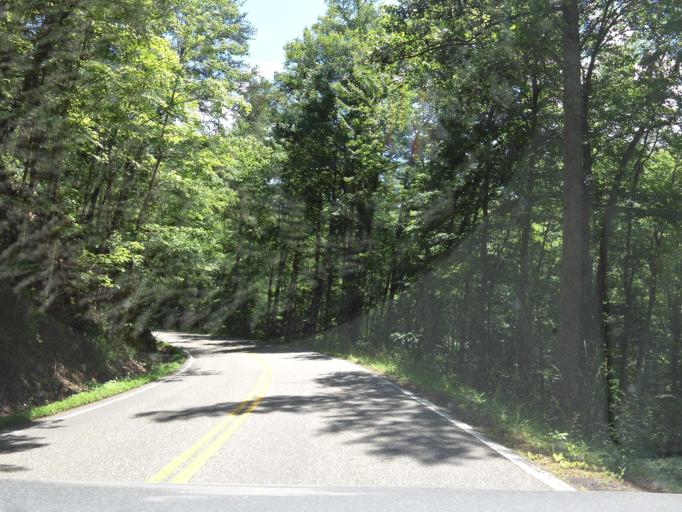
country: US
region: North Carolina
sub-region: Graham County
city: Robbinsville
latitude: 35.4852
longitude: -83.9320
